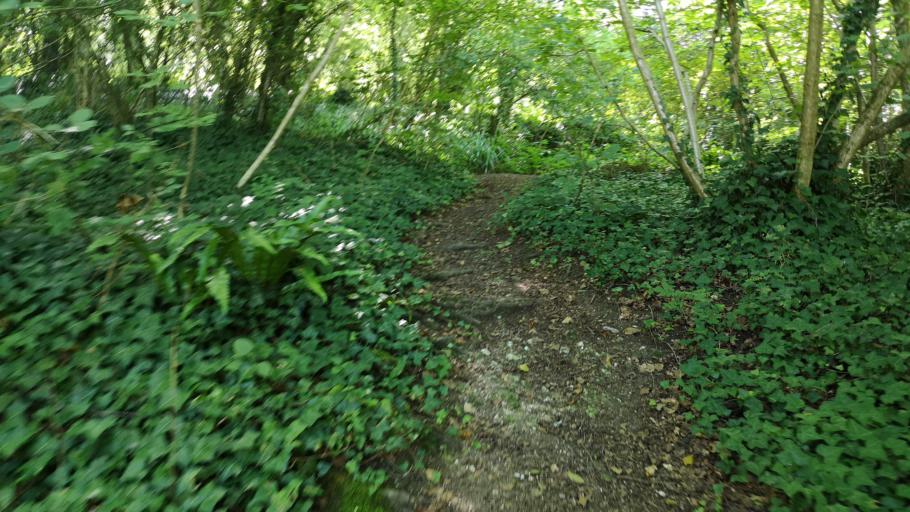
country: GB
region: England
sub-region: Isle of Wight
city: Brading
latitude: 50.6815
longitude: -1.1600
